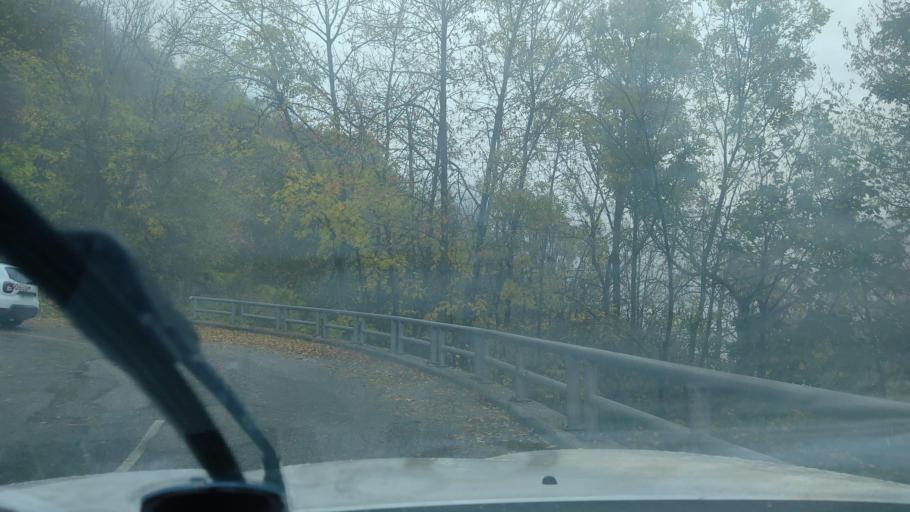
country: FR
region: Rhone-Alpes
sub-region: Departement de la Savoie
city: Bozel
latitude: 45.4497
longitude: 6.6585
